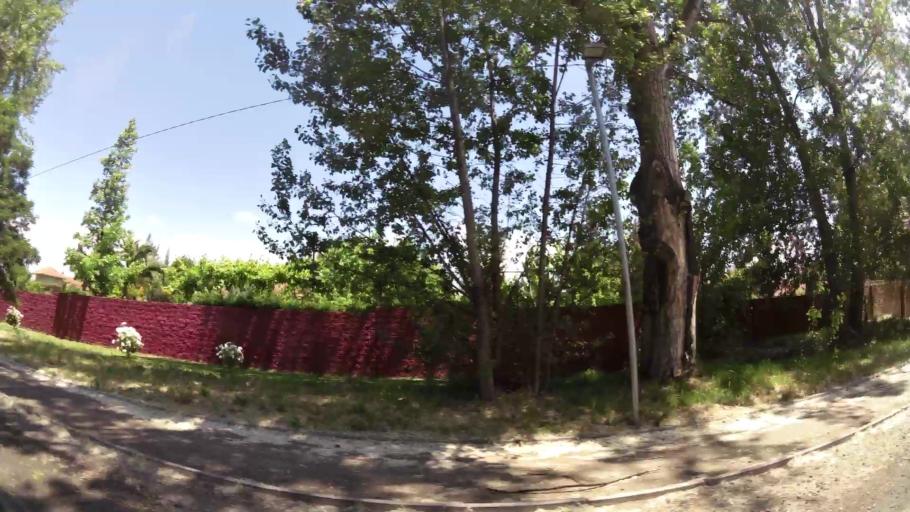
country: CL
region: Santiago Metropolitan
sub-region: Provincia de Maipo
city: San Bernardo
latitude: -33.5749
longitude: -70.7701
